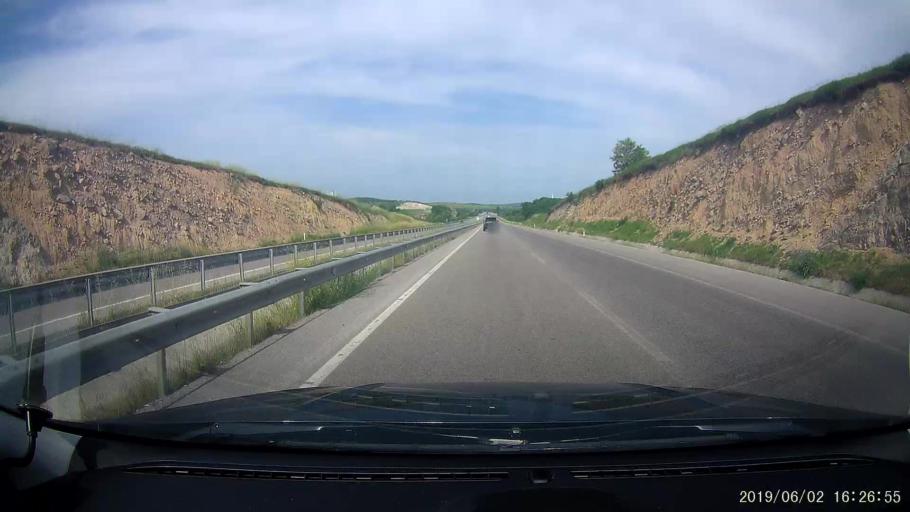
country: TR
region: Samsun
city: Ladik
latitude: 41.0017
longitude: 35.8155
